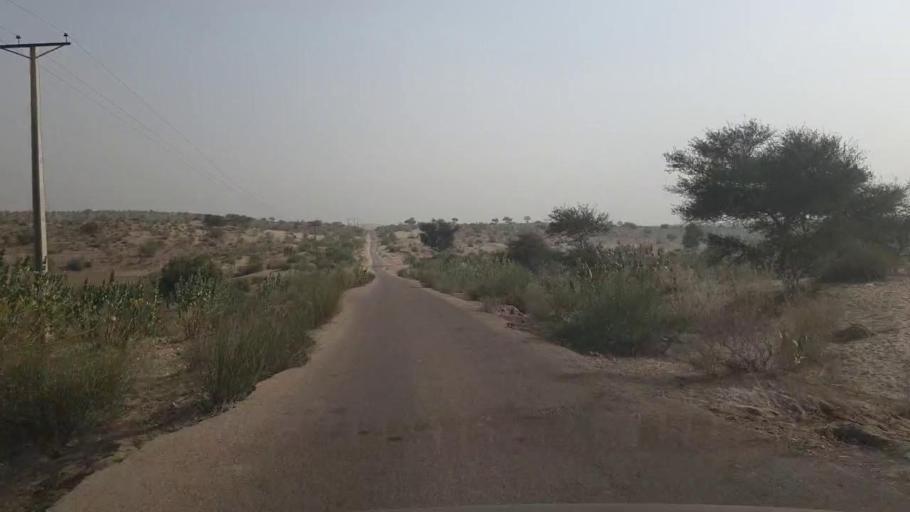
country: PK
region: Sindh
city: Chor
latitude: 25.5551
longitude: 69.9581
